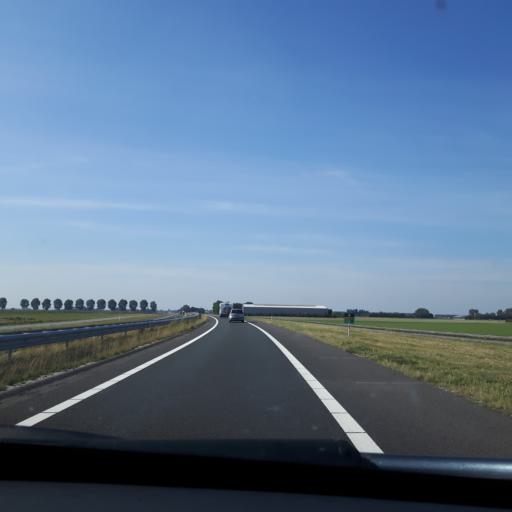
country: NL
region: Zeeland
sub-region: Gemeente Borsele
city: Borssele
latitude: 51.3258
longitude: 3.6750
